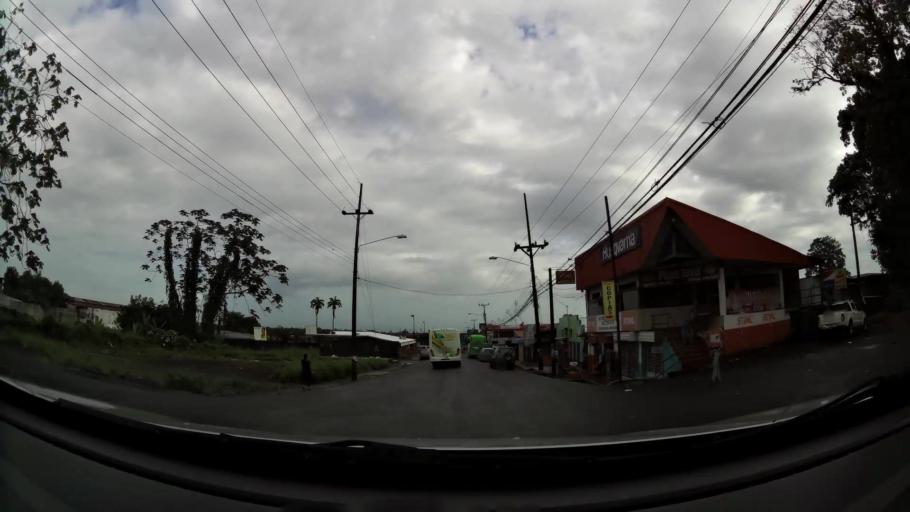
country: CR
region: Limon
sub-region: Canton de Siquirres
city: Siquirres
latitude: 10.0948
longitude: -83.5067
